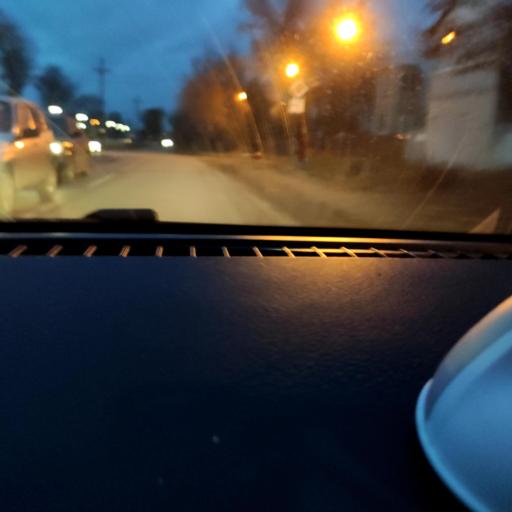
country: RU
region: Samara
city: Petra-Dubrava
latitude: 53.2531
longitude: 50.3386
